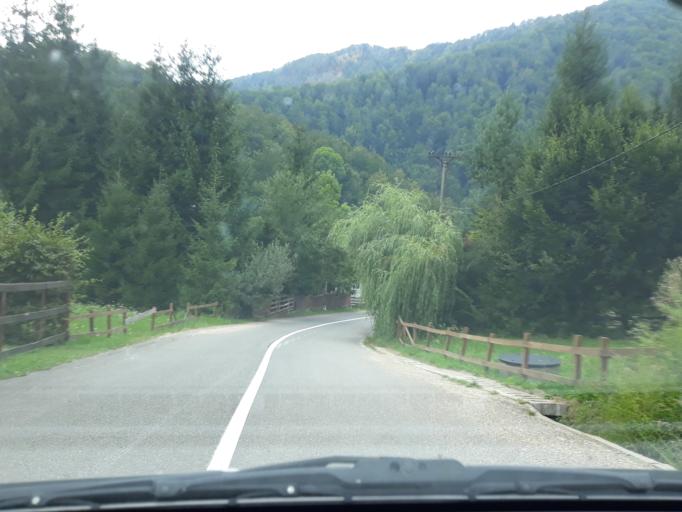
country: RO
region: Bihor
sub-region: Comuna Pietroasa
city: Pietroasa
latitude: 46.6026
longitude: 22.6482
